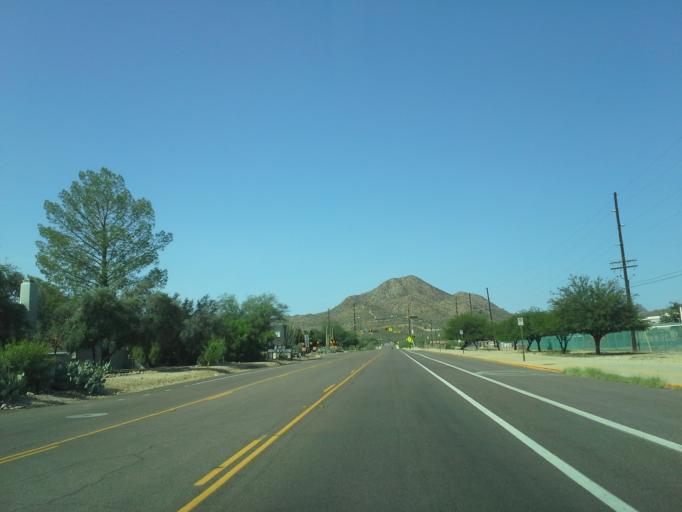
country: US
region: Arizona
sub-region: Pima County
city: South Tucson
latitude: 32.2250
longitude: -111.0261
